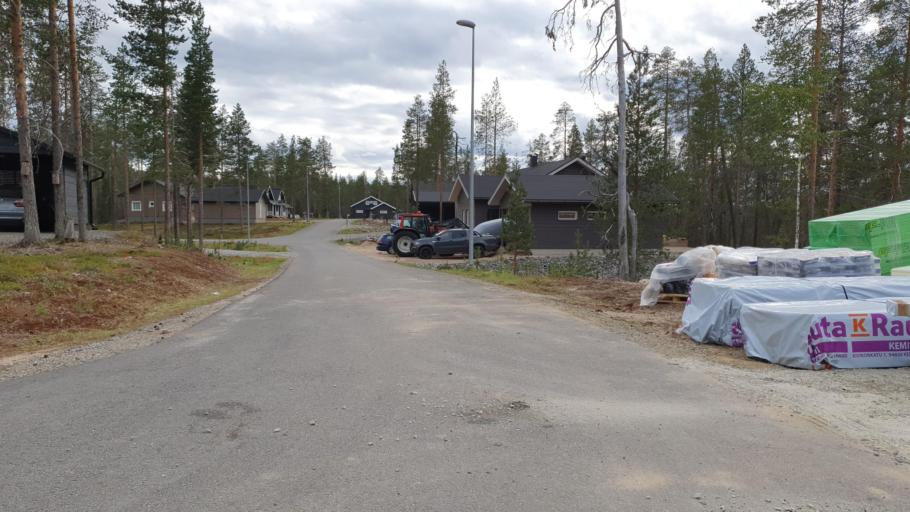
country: FI
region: Lapland
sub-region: Tunturi-Lappi
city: Kolari
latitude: 67.5990
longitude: 24.1336
